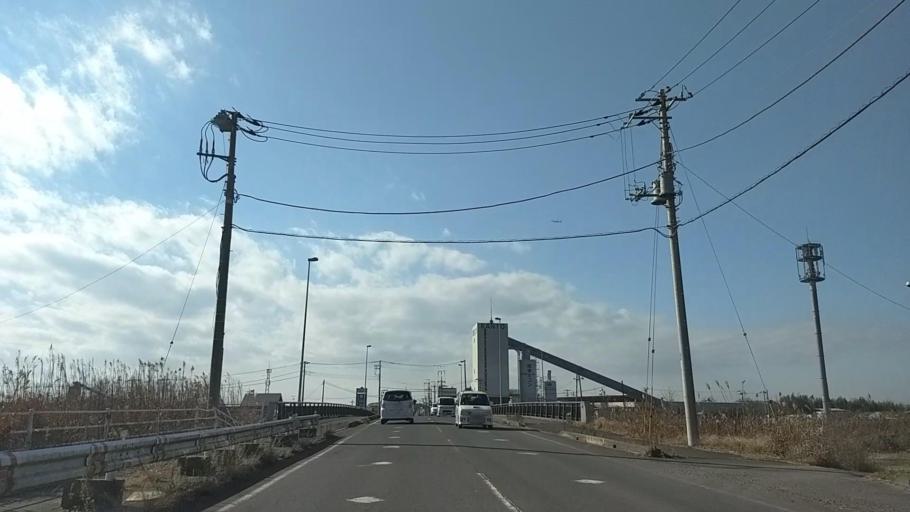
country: JP
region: Chiba
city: Yokaichiba
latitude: 35.6665
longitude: 140.4954
